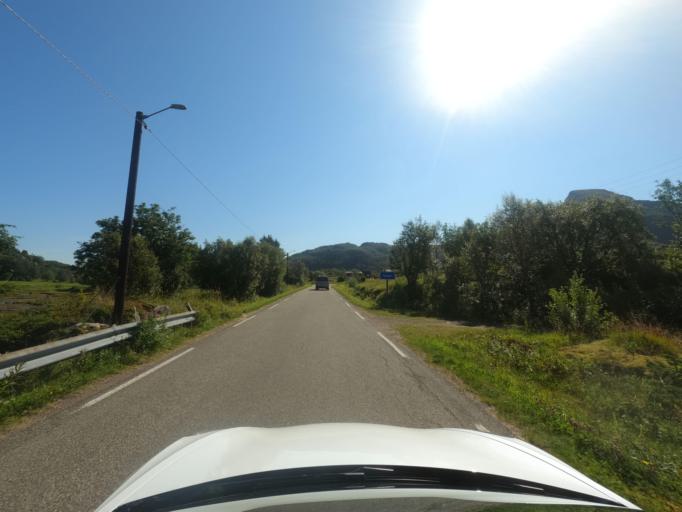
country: NO
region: Nordland
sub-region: Hadsel
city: Stokmarknes
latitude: 68.3034
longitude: 15.0136
